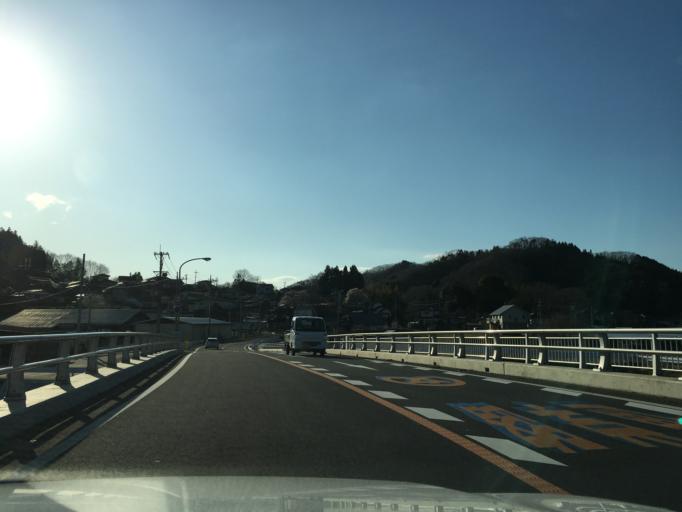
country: JP
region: Ibaraki
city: Daigo
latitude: 36.7779
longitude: 140.3450
